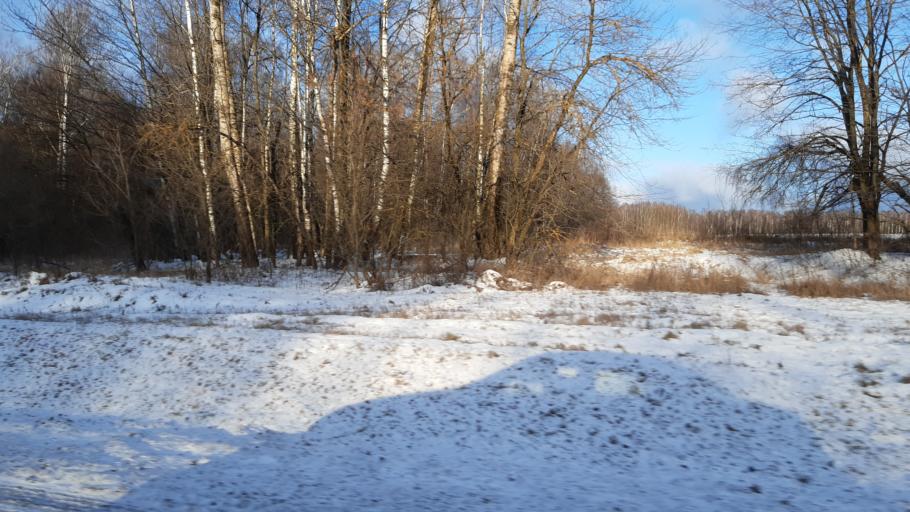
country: RU
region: Vladimir
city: Arsaki
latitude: 56.2910
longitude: 38.3818
